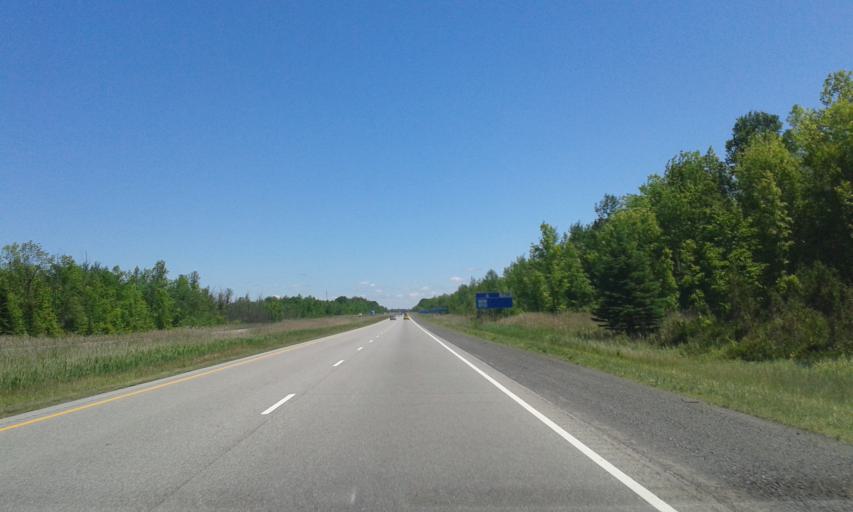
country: US
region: New York
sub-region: St. Lawrence County
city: Ogdensburg
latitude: 44.8406
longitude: -75.3571
